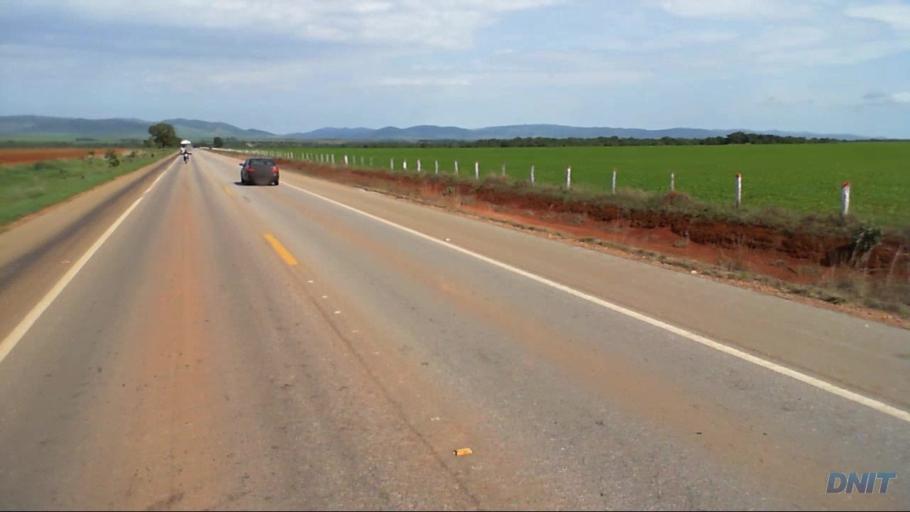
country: BR
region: Goias
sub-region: Barro Alto
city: Barro Alto
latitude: -15.1105
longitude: -48.8435
